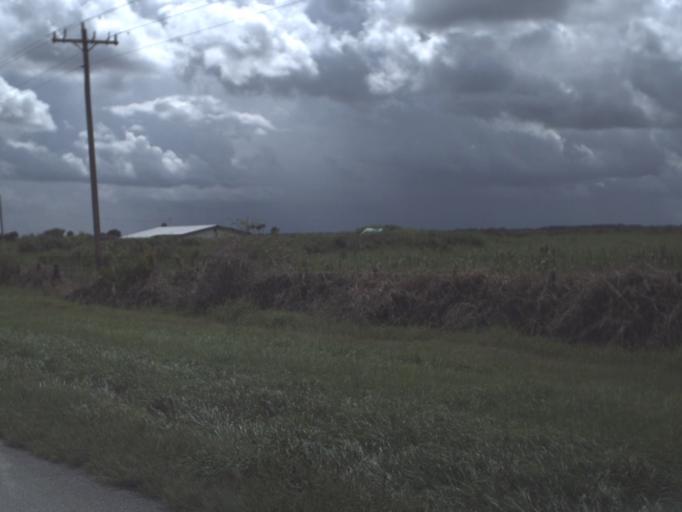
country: US
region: Florida
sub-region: Okeechobee County
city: Okeechobee
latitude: 27.3563
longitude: -80.9599
